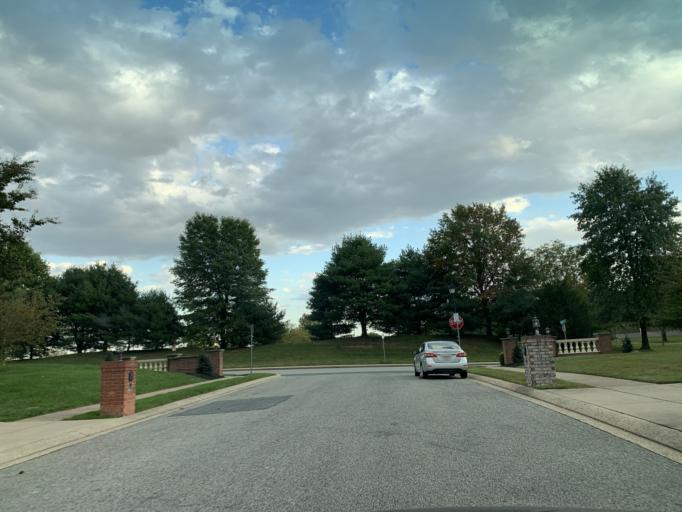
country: US
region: Maryland
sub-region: Harford County
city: Bel Air South
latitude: 39.5092
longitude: -76.3240
